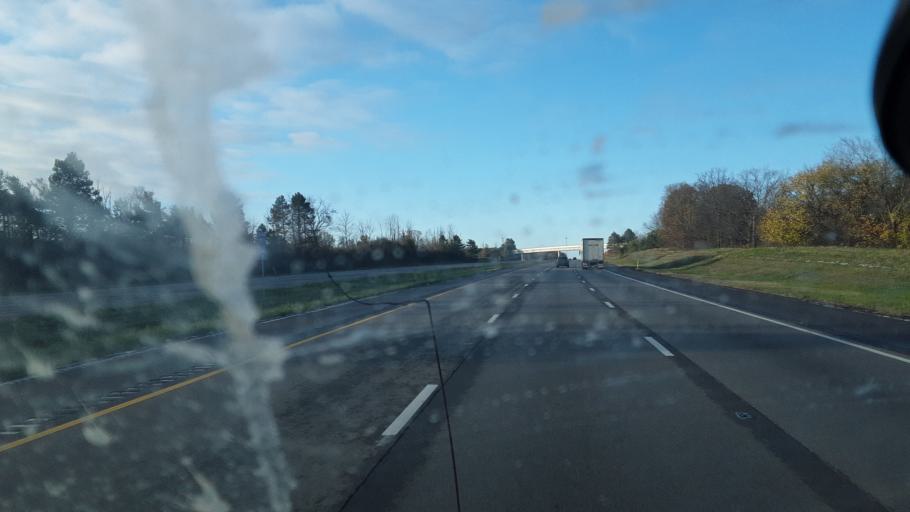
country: US
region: Ohio
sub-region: Wayne County
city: West Salem
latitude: 40.9715
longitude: -82.0505
